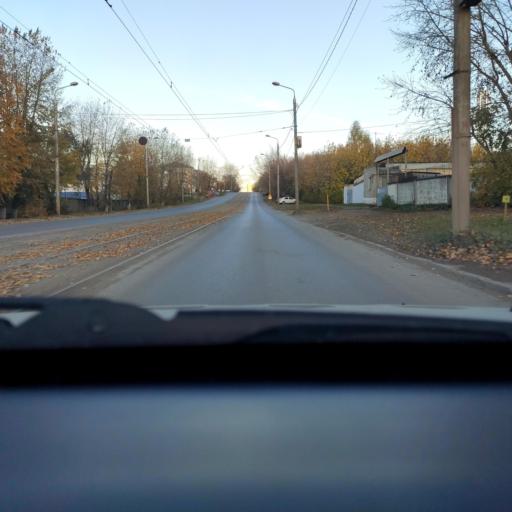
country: RU
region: Perm
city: Kondratovo
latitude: 58.0071
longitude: 56.1676
